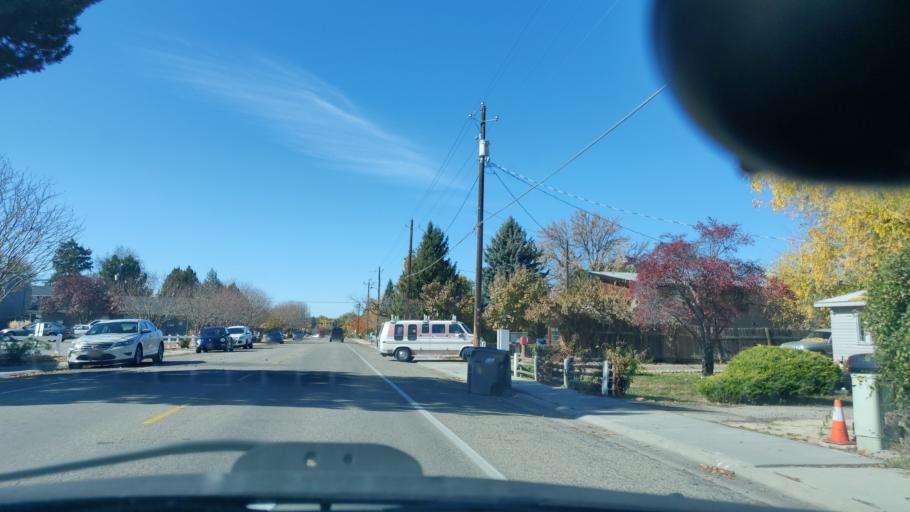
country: US
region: Idaho
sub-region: Ada County
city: Garden City
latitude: 43.5934
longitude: -116.2400
